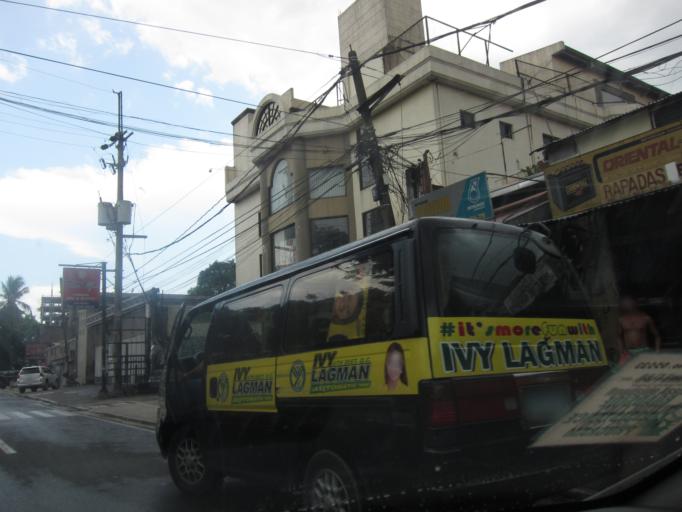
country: PH
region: Metro Manila
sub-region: Quezon City
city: Quezon City
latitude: 14.6407
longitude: 121.0548
